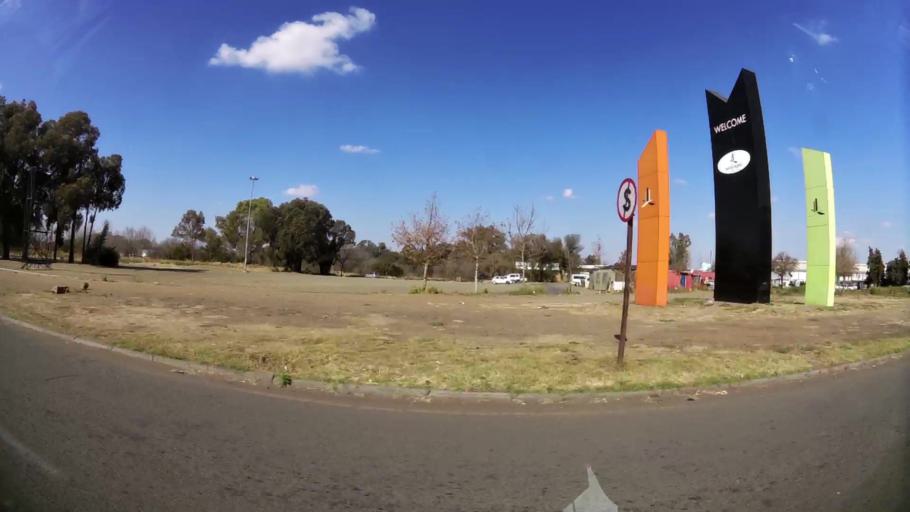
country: ZA
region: Orange Free State
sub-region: Mangaung Metropolitan Municipality
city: Bloemfontein
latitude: -29.1177
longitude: 26.2371
